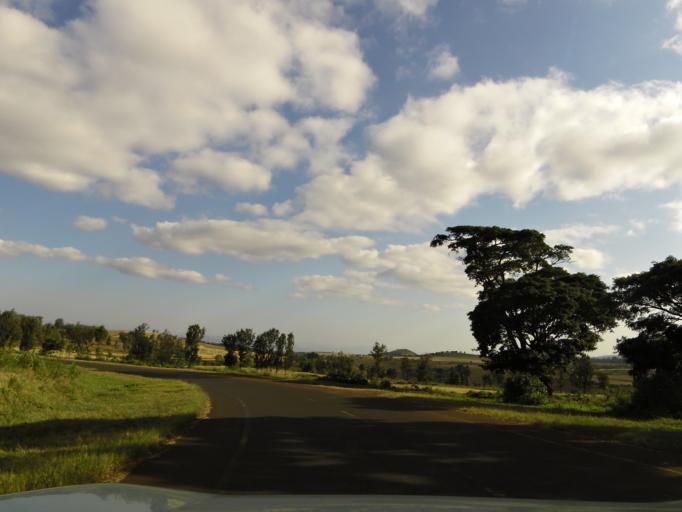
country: TZ
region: Arusha
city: Kiratu
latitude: -3.3129
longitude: 35.5927
